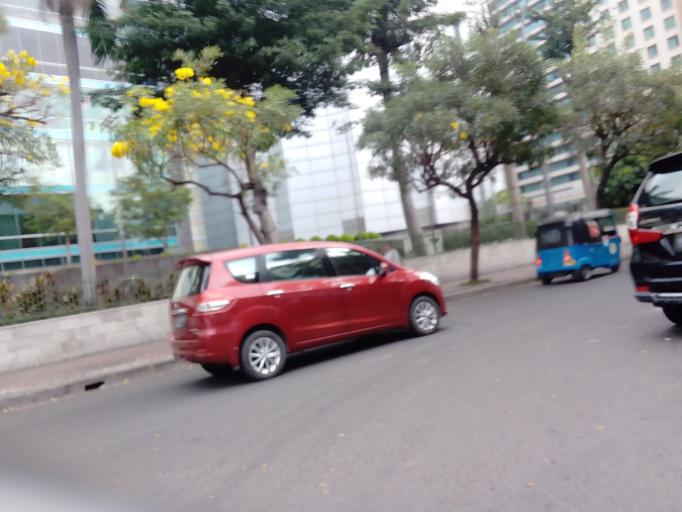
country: ID
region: Jakarta Raya
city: Jakarta
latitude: -6.1941
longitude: 106.8197
